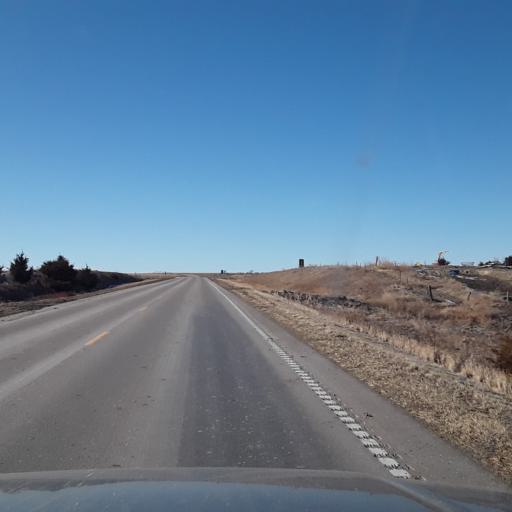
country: US
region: Nebraska
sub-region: Dawson County
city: Gothenburg
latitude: 40.7058
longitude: -100.2245
